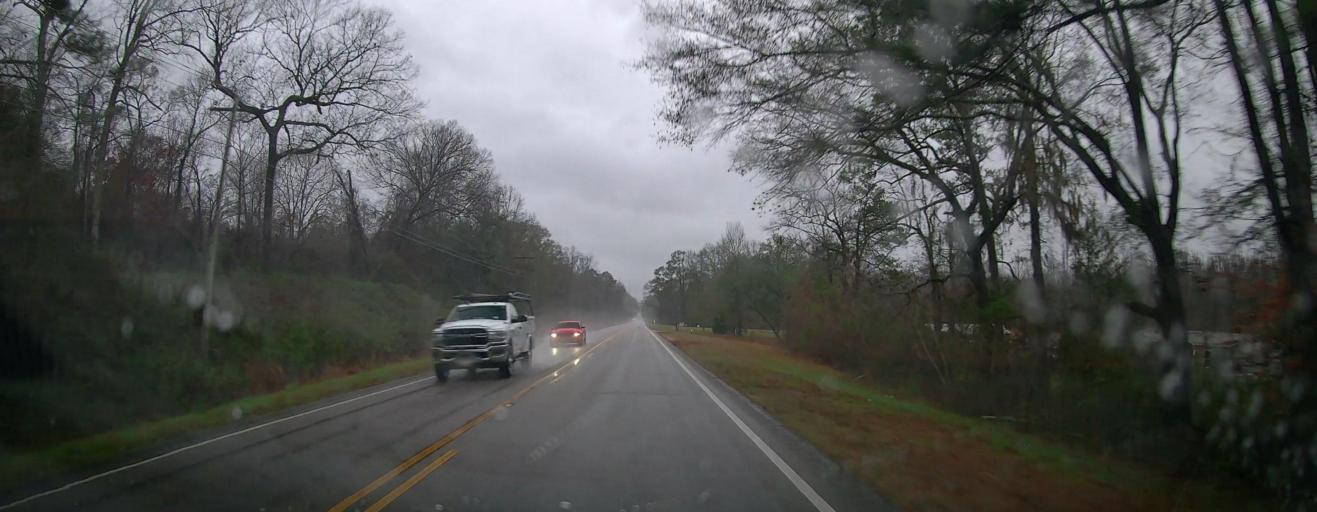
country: US
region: Alabama
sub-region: Autauga County
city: Prattville
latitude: 32.4787
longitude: -86.5278
